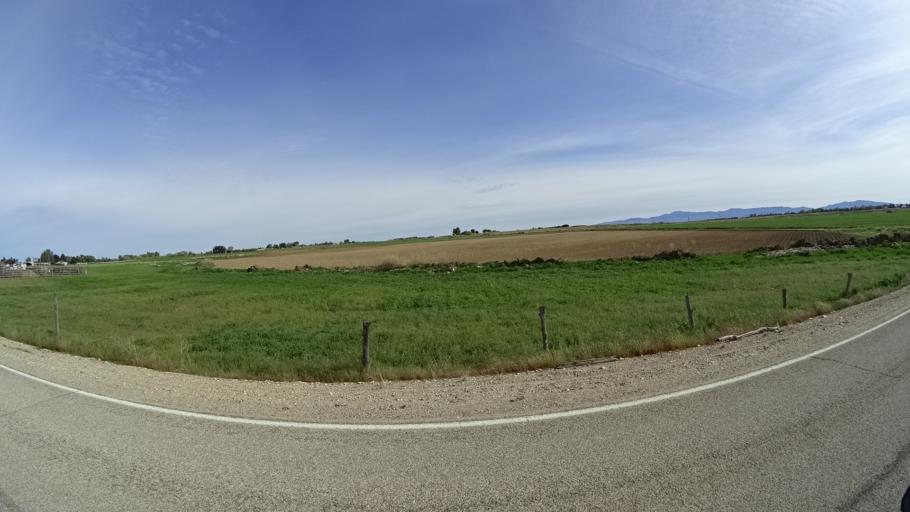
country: US
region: Idaho
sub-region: Ada County
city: Kuna
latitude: 43.4736
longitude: -116.3477
